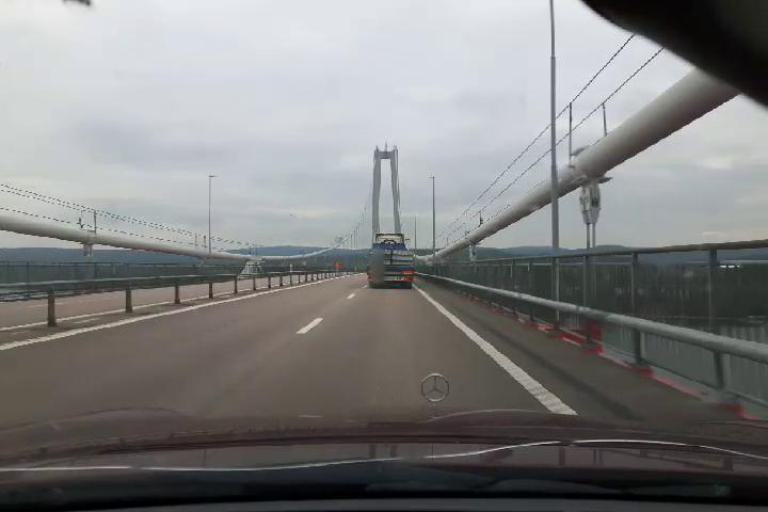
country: SE
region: Vaesternorrland
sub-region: Haernoesands Kommun
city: Haernoesand
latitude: 62.7960
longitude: 17.9350
